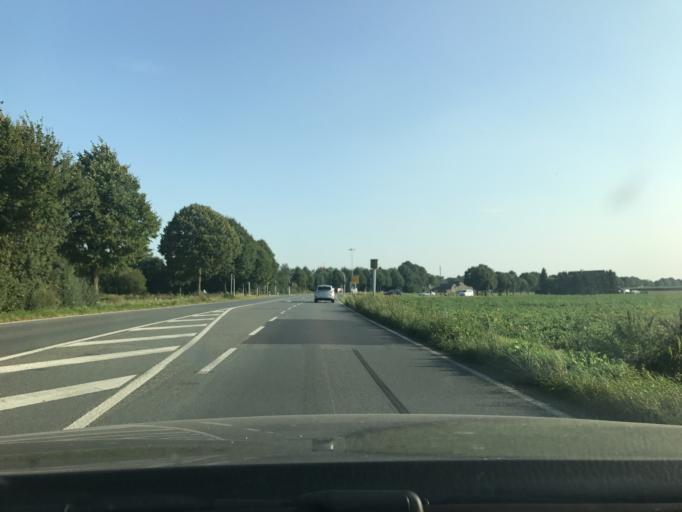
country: DE
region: North Rhine-Westphalia
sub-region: Regierungsbezirk Dusseldorf
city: Uedem
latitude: 51.6753
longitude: 6.2700
